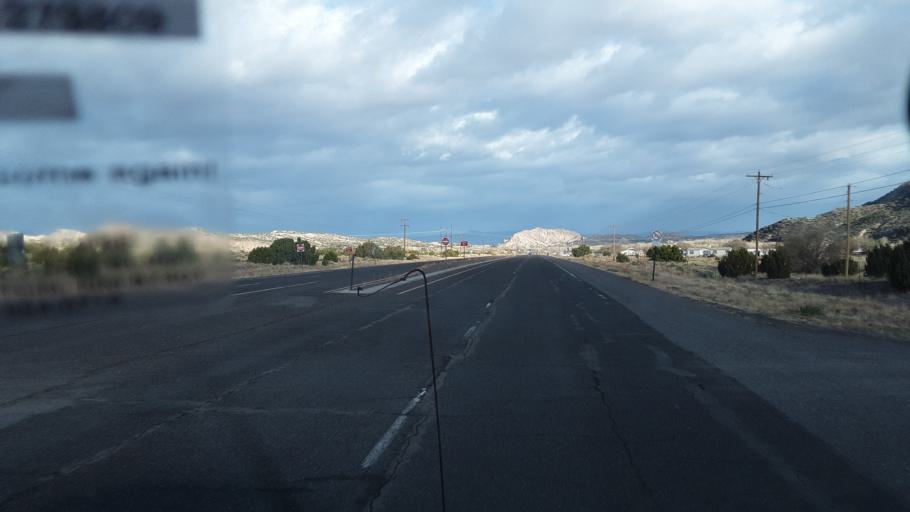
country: US
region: New Mexico
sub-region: Rio Arriba County
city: Ohkay Owingeh
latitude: 36.0756
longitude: -106.1266
